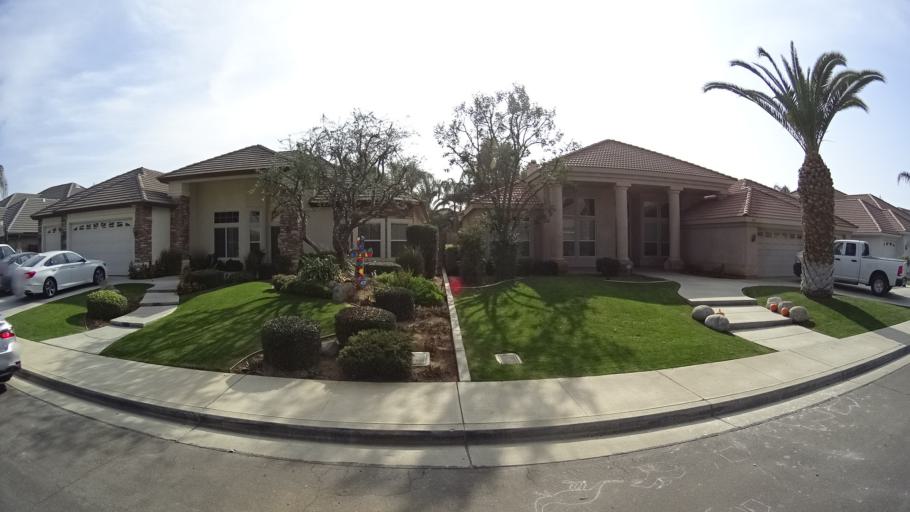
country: US
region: California
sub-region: Kern County
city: Greenacres
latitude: 35.4192
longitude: -119.1028
